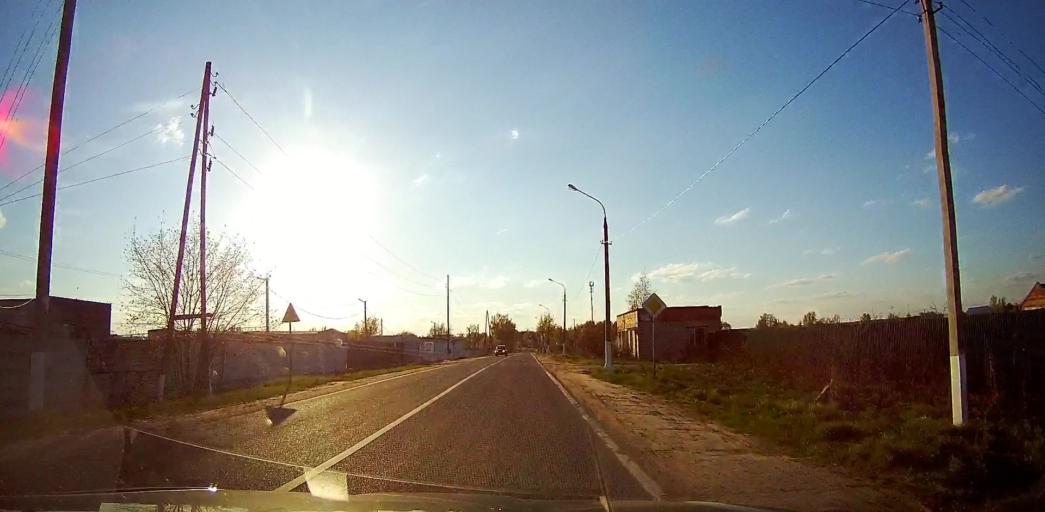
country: RU
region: Moskovskaya
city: Malino
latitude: 55.2771
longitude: 38.1663
